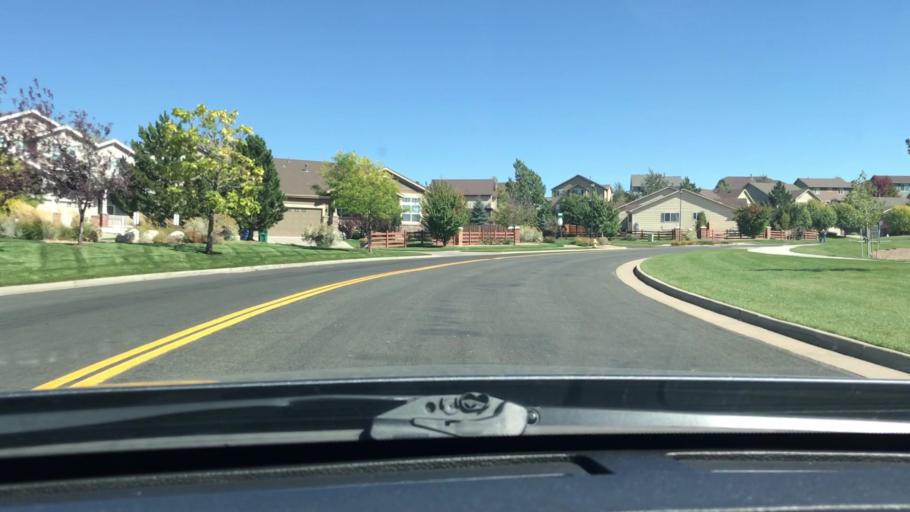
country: US
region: Colorado
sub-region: Arapahoe County
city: Dove Valley
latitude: 39.6428
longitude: -104.7412
